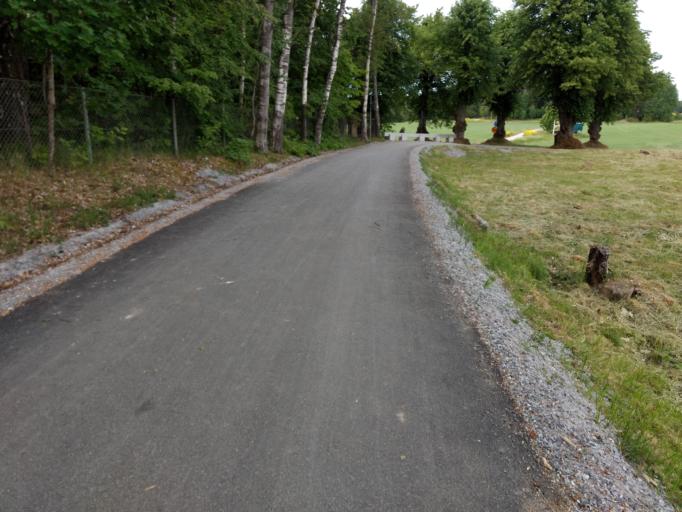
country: SE
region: Stockholm
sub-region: Upplands Vasby Kommun
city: Upplands Vaesby
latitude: 59.5340
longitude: 17.9142
